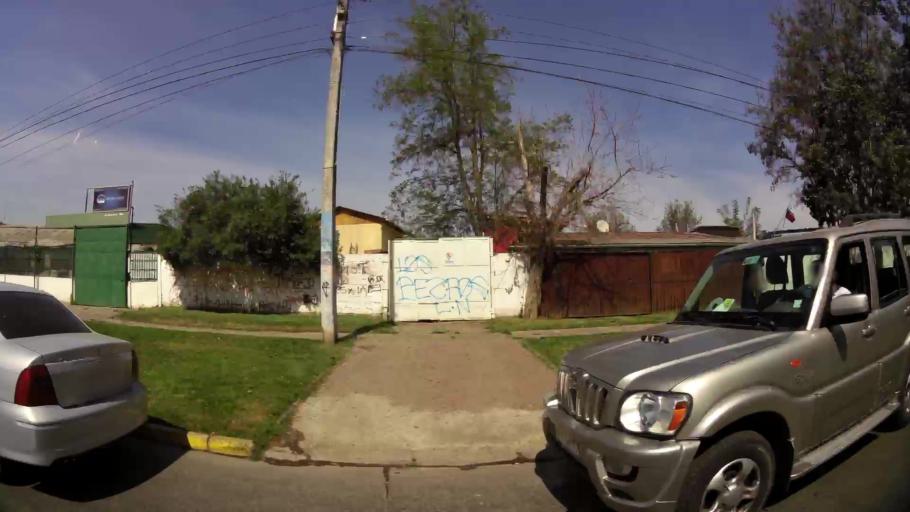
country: CL
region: Santiago Metropolitan
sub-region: Provincia de Santiago
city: Lo Prado
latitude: -33.4351
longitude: -70.7287
